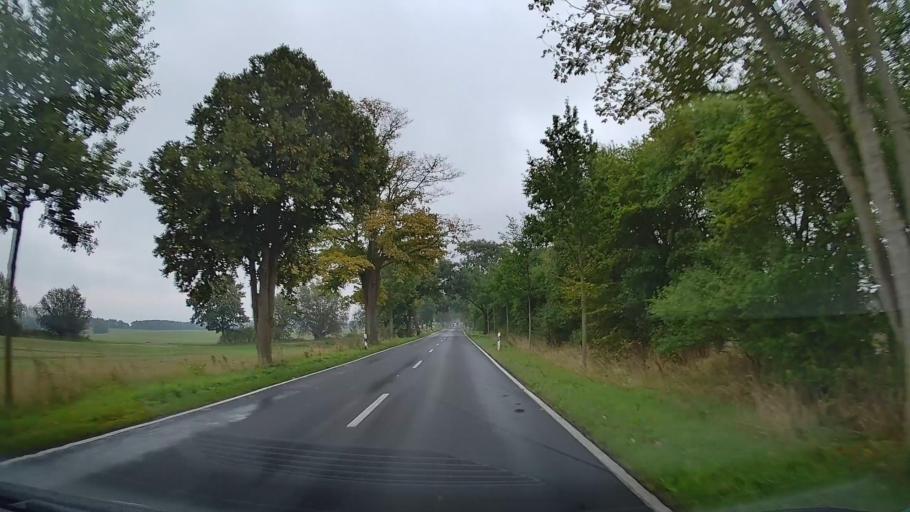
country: DE
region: Mecklenburg-Vorpommern
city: Ostseebad Boltenhagen
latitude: 53.9478
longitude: 11.2336
